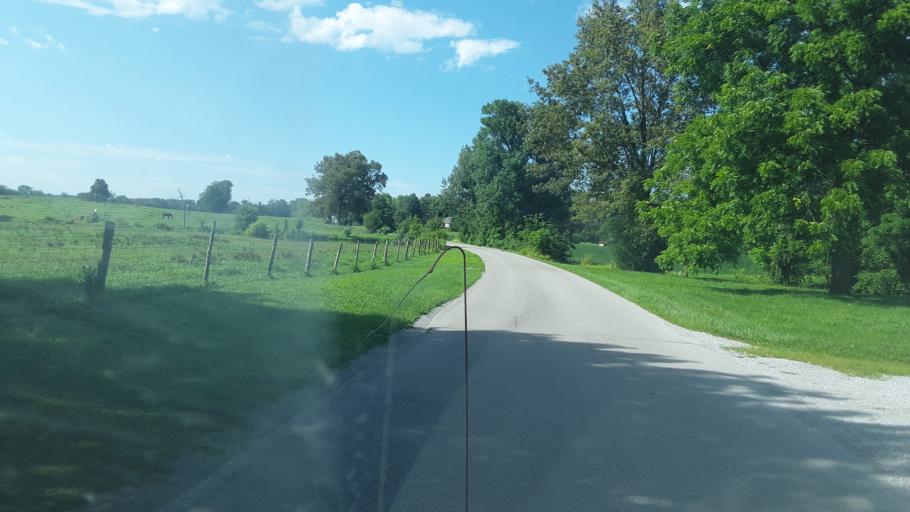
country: US
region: Kentucky
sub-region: Todd County
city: Elkton
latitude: 36.7383
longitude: -87.1676
